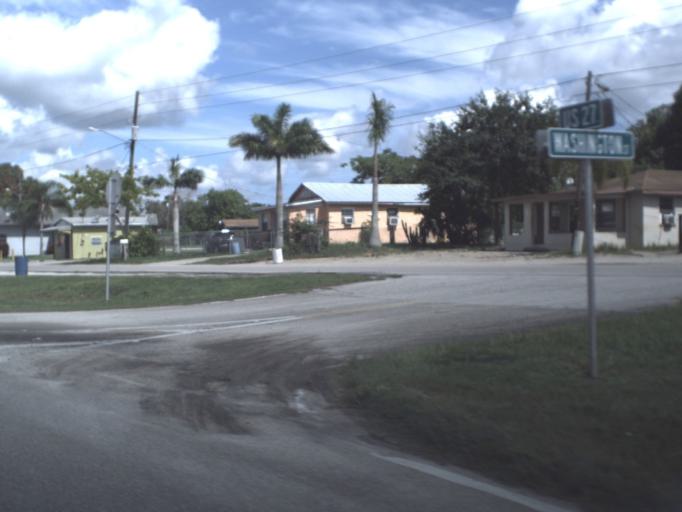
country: US
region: Florida
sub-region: Highlands County
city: Lake Placid
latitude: 27.2773
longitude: -81.3531
